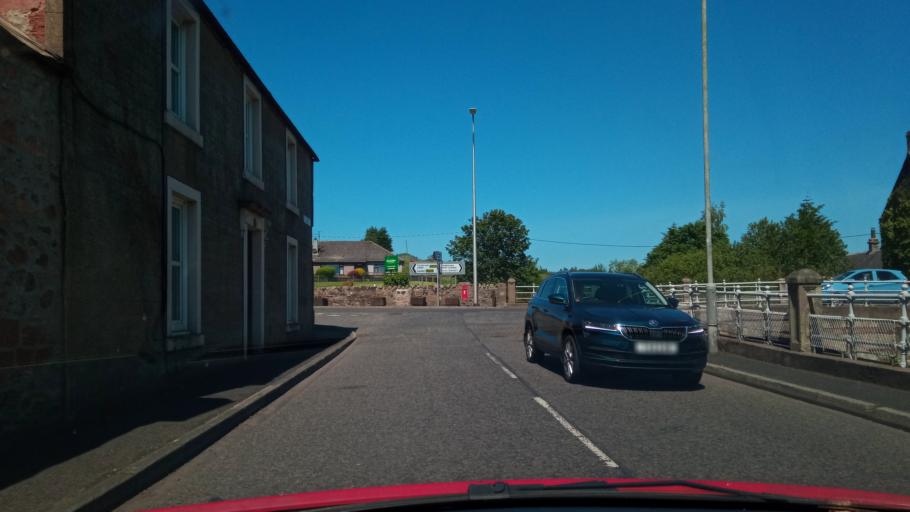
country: GB
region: Scotland
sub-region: The Scottish Borders
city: Kelso
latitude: 55.7058
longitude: -2.4651
